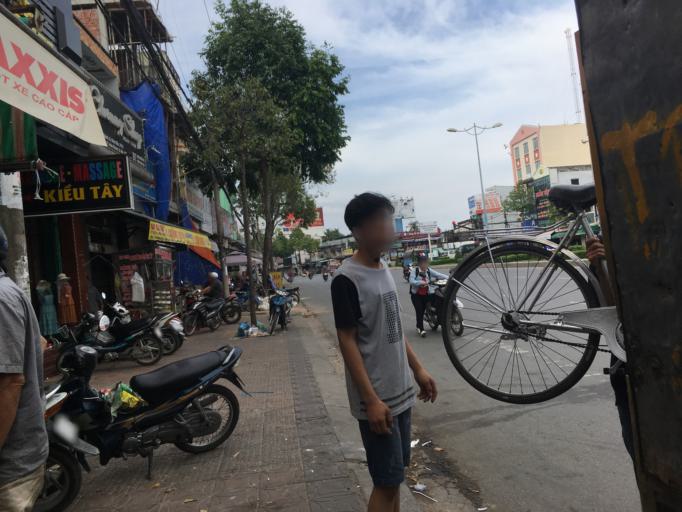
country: VN
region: Can Tho
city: Can Tho
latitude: 10.0319
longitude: 105.7737
